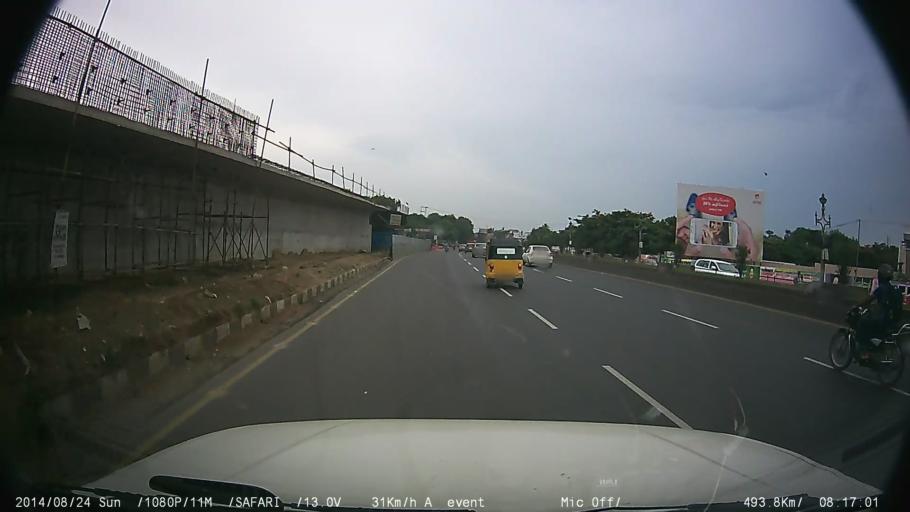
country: IN
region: Tamil Nadu
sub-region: Kancheepuram
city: Saint Thomas Mount
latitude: 12.9963
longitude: 80.1895
